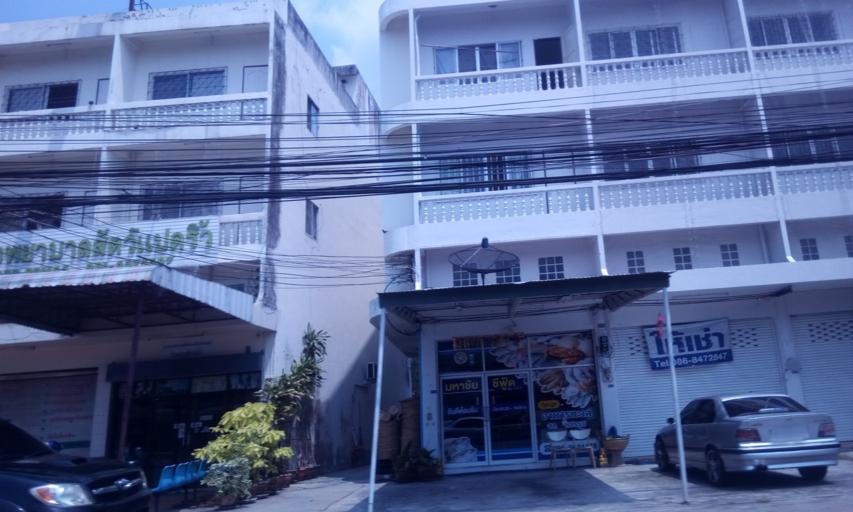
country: TH
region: Chachoengsao
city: Chachoengsao
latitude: 13.6716
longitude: 101.0846
